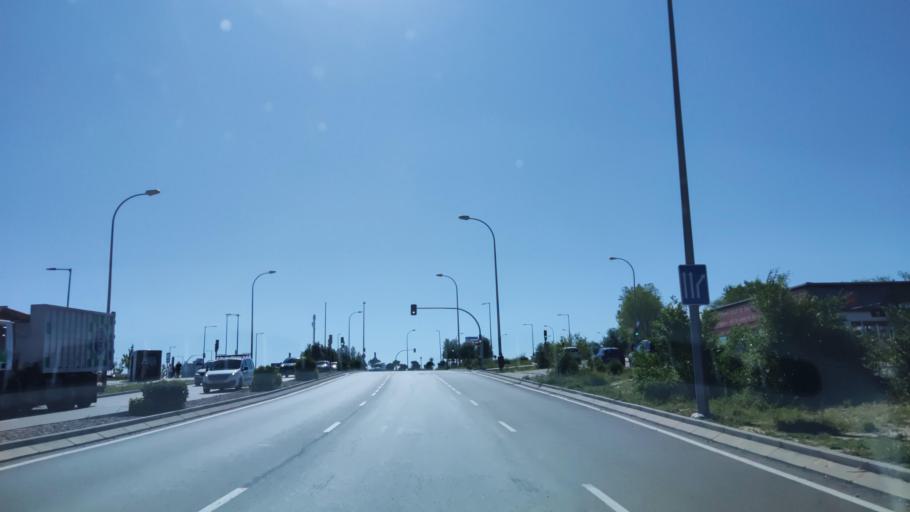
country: ES
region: Madrid
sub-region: Provincia de Madrid
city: San Blas
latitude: 40.4334
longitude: -3.6021
